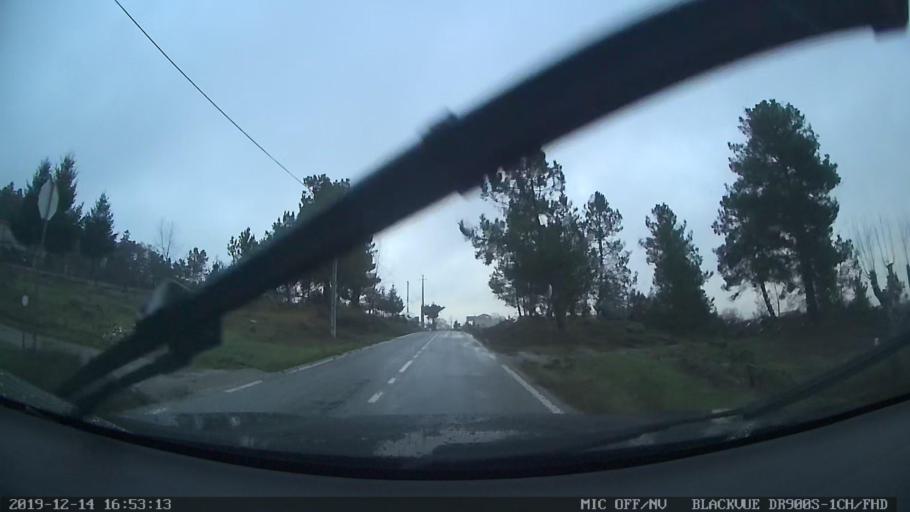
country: PT
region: Vila Real
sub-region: Murca
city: Murca
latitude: 41.4290
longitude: -7.5164
